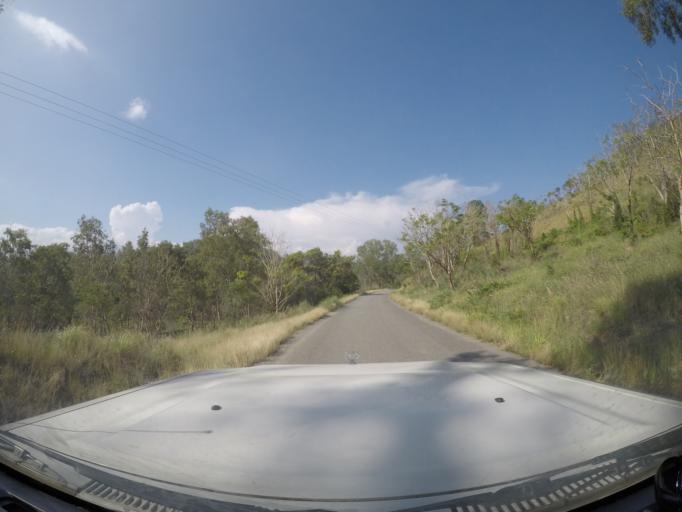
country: PG
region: Central Province
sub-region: Rigo
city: Kwikila
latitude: -9.8598
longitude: 147.5633
